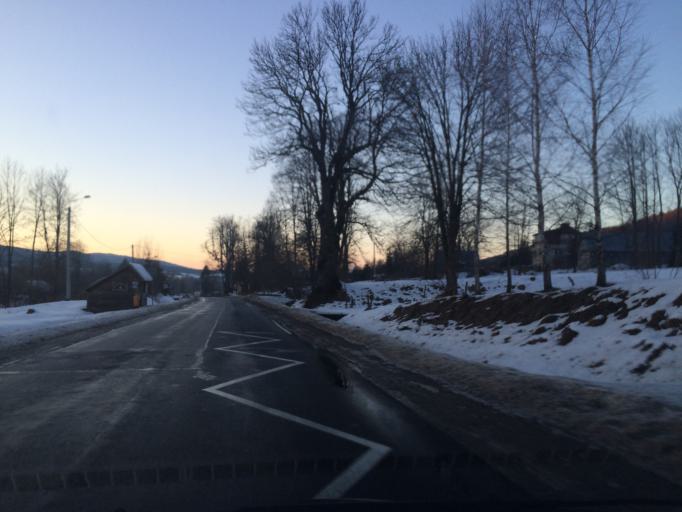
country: PL
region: Subcarpathian Voivodeship
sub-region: Powiat bieszczadzki
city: Czarna
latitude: 49.3648
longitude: 22.6631
